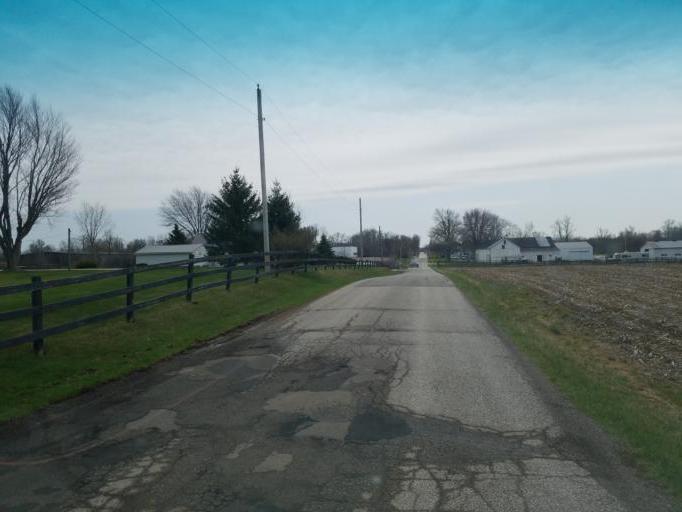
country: US
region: Ohio
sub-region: Crawford County
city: Galion
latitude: 40.7358
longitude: -82.7410
